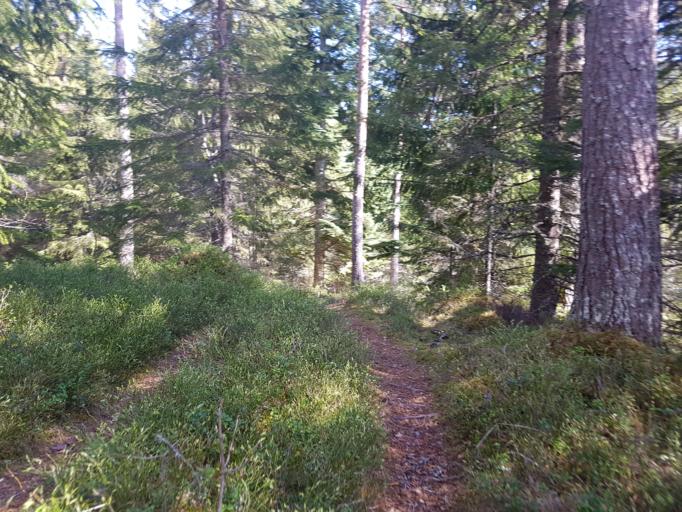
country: NO
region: Sor-Trondelag
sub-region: Trondheim
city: Trondheim
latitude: 63.4209
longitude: 10.3198
